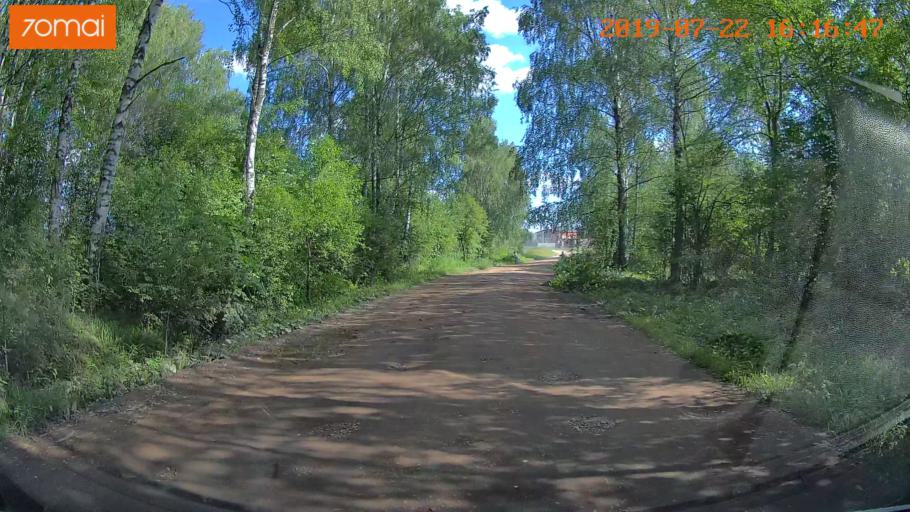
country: RU
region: Ivanovo
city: Novo-Talitsy
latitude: 57.0708
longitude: 40.8822
